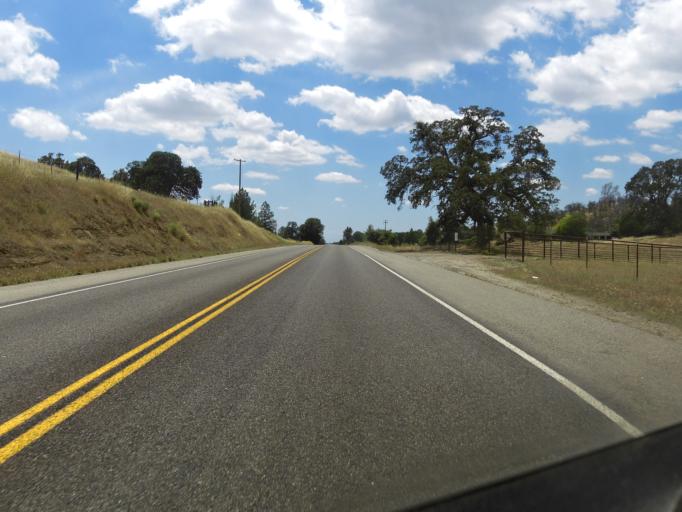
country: US
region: California
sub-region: Madera County
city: Yosemite Lakes
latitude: 37.1428
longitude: -119.6774
